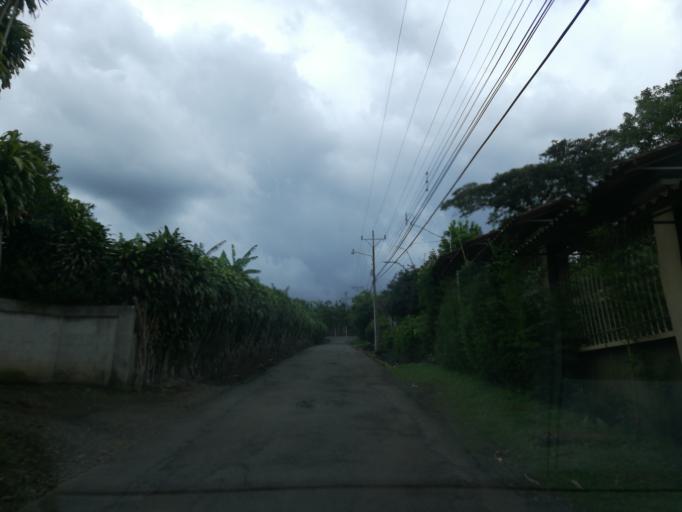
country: CR
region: Heredia
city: Santo Domingo
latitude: 10.0388
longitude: -84.1812
